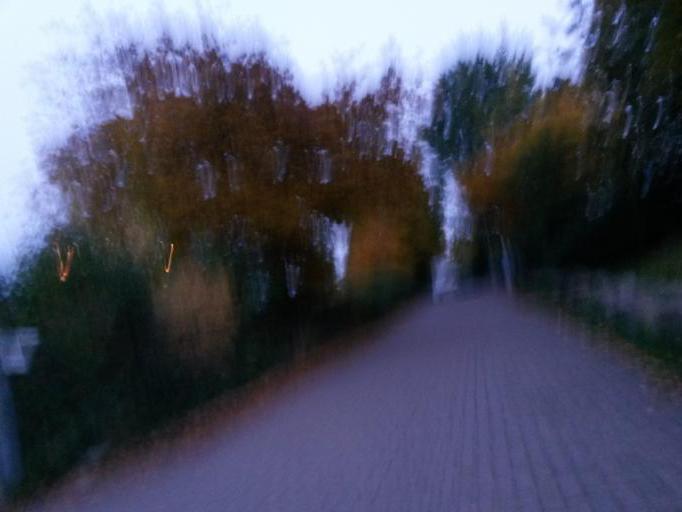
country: DE
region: Bremen
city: Bremen
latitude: 53.0617
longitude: 8.8423
